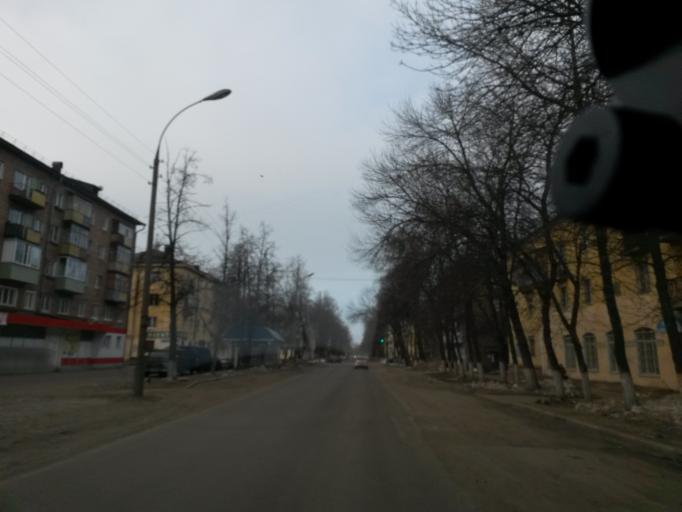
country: RU
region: Jaroslavl
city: Yaroslavl
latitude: 57.6365
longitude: 39.8481
